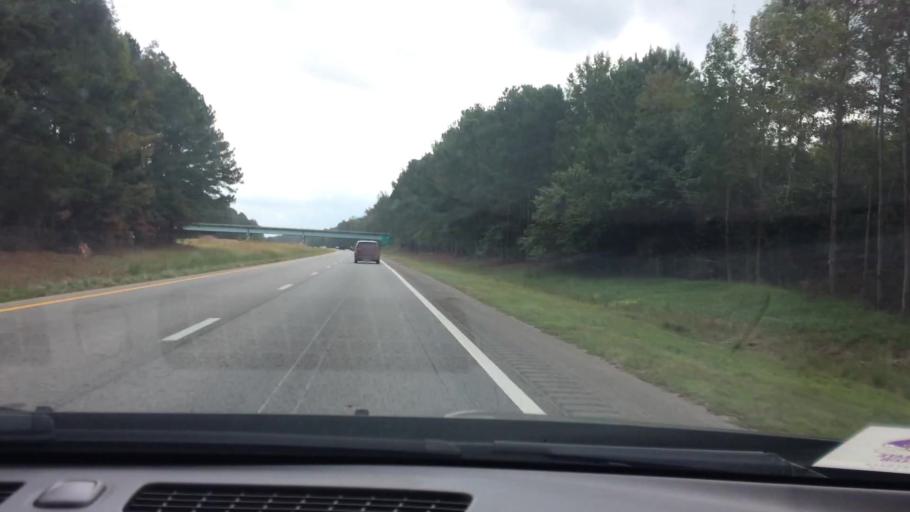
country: US
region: North Carolina
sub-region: Nash County
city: Spring Hope
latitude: 35.7902
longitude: -78.1417
